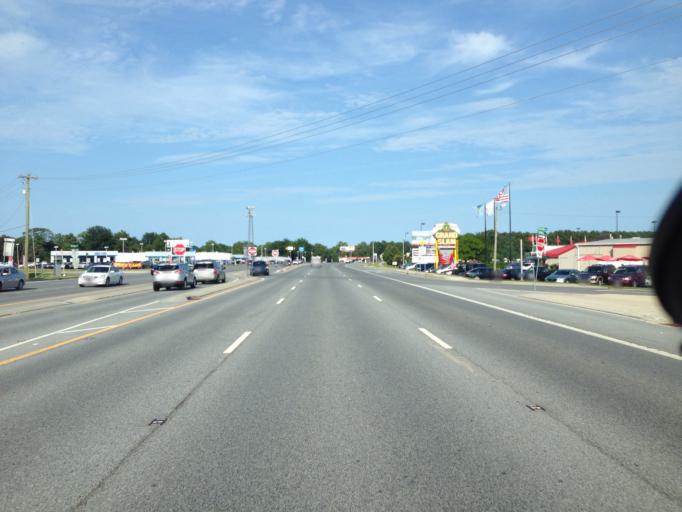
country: US
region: Delaware
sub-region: Sussex County
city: Lewes
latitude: 38.7485
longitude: -75.1658
